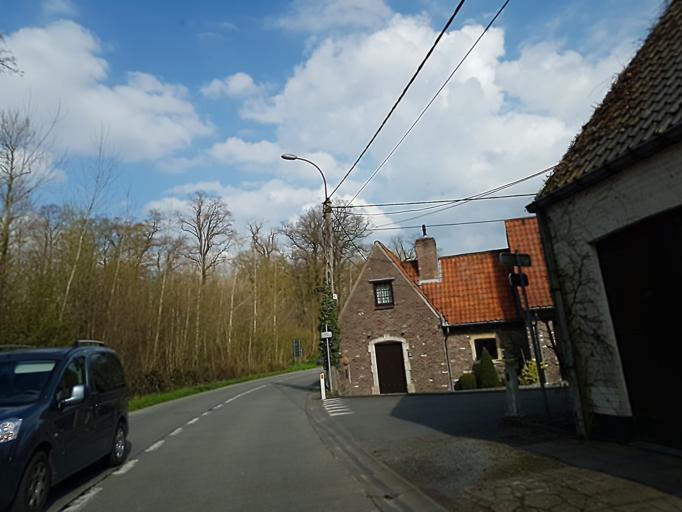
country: BE
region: Flanders
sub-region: Provincie Oost-Vlaanderen
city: Oudenaarde
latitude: 50.8482
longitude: 3.5761
